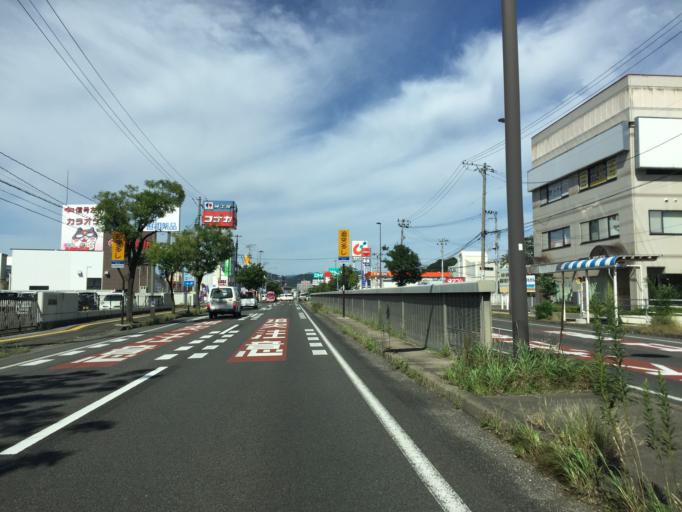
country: JP
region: Fukushima
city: Fukushima-shi
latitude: 37.7315
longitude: 140.4666
